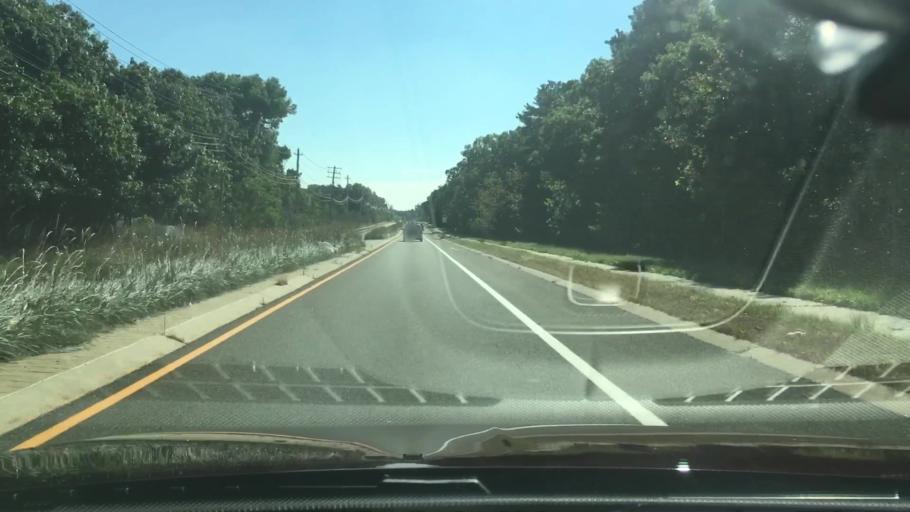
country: US
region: New York
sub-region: Suffolk County
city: Coram
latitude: 40.8978
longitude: -73.0203
